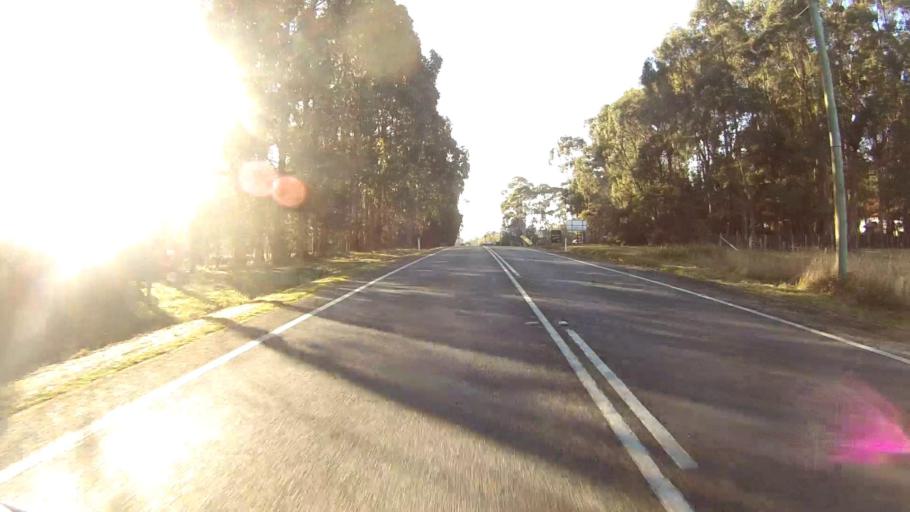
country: AU
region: Tasmania
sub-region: Clarence
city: Sandford
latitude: -43.0592
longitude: 147.8649
